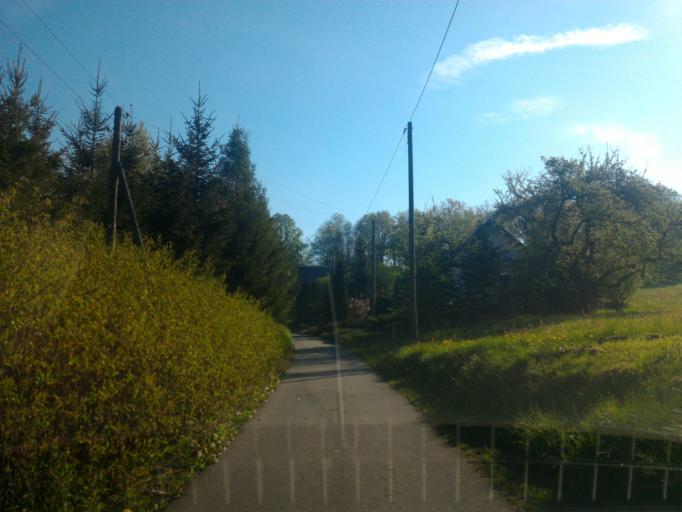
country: DE
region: Saxony
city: Leutersdorf
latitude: 50.9438
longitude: 14.6305
